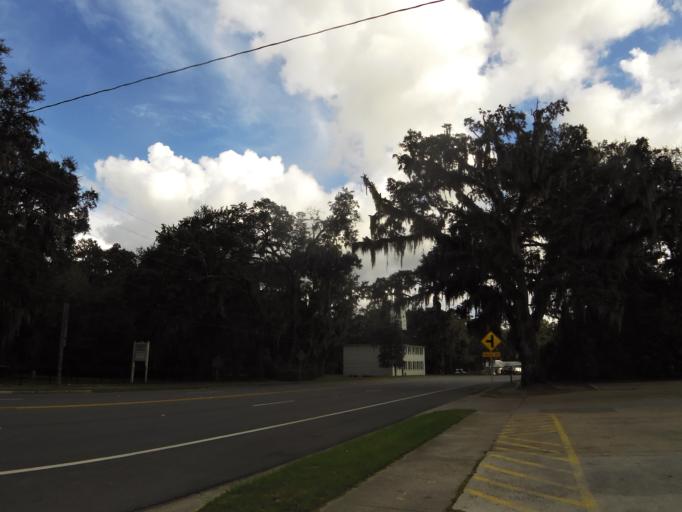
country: US
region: Georgia
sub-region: Liberty County
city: Midway
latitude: 31.8071
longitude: -81.4308
